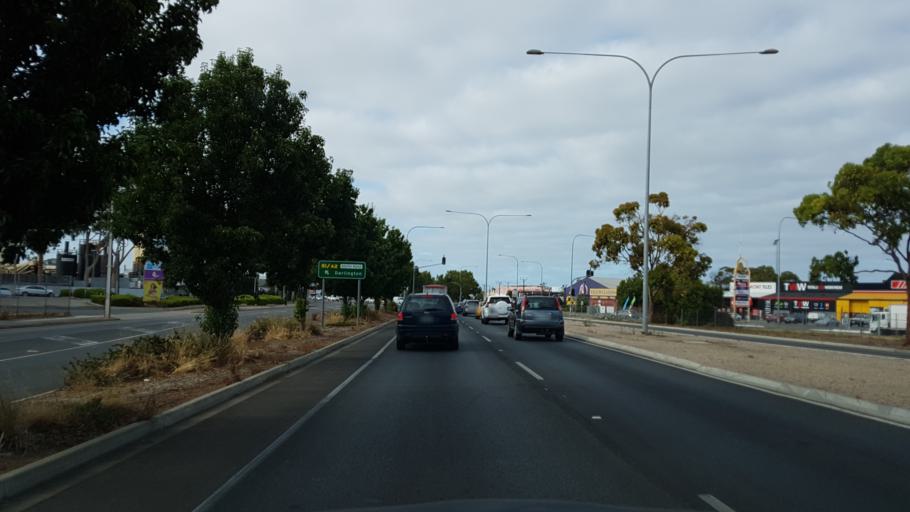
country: AU
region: South Australia
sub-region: Unley
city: Forestville
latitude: -34.9363
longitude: 138.5716
